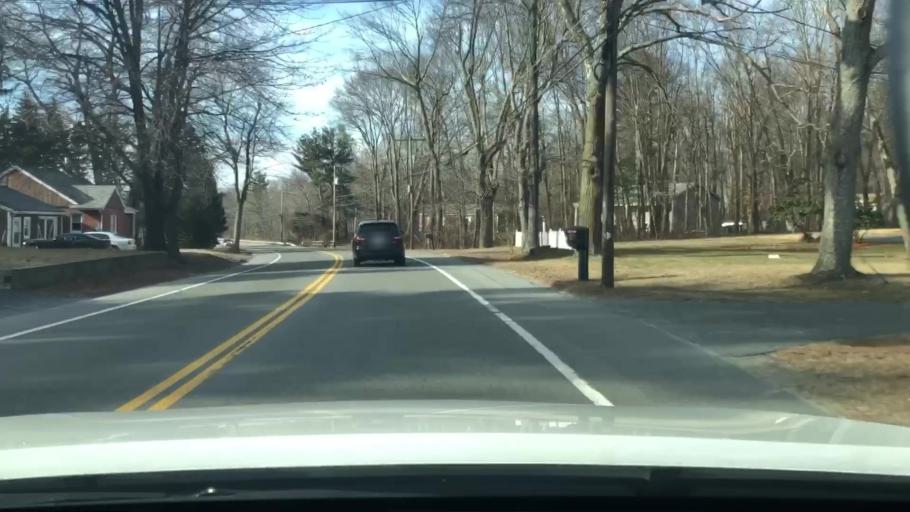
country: US
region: Massachusetts
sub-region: Worcester County
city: Grafton
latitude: 42.2058
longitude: -71.6746
